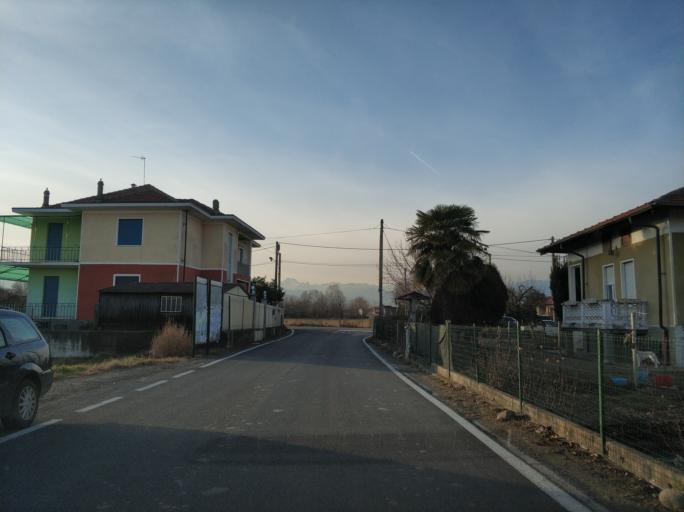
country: IT
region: Piedmont
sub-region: Provincia di Torino
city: San Francesco al Campo
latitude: 45.2250
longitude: 7.6419
